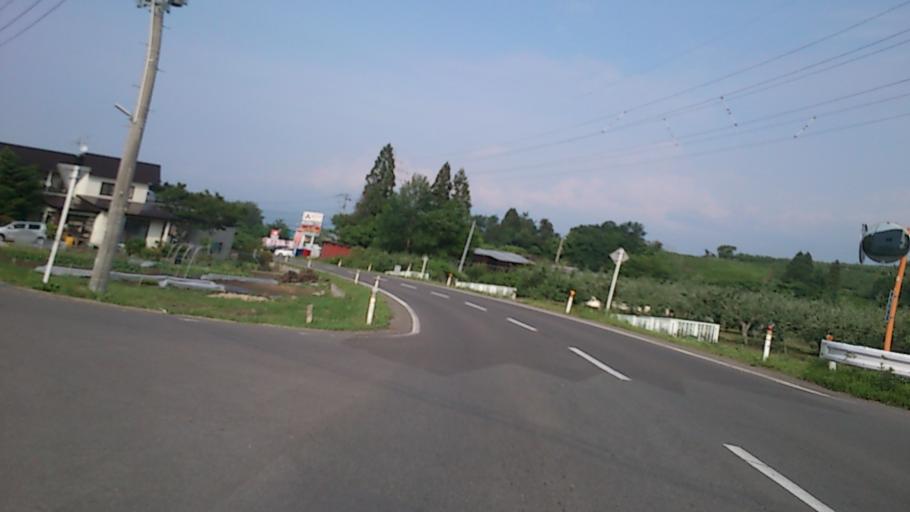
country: JP
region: Aomori
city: Hirosaki
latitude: 40.5573
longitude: 140.4842
